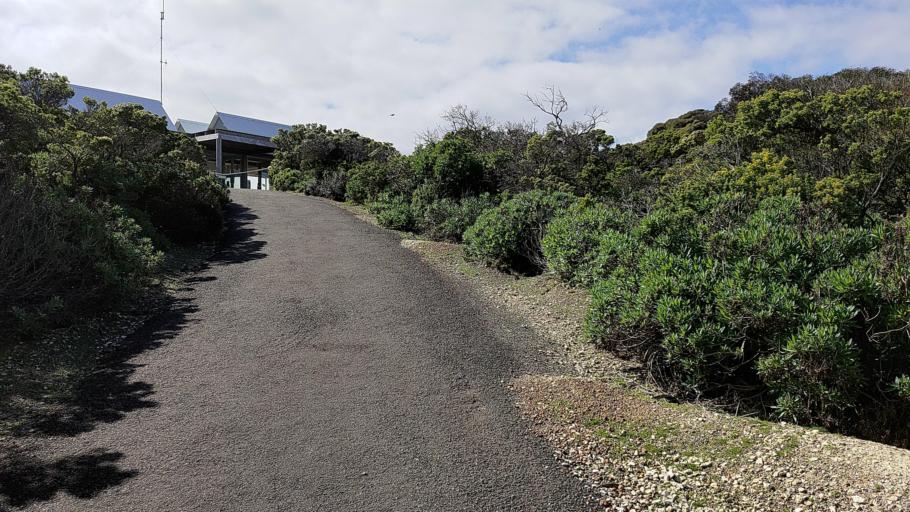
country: AU
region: South Australia
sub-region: Kangaroo Island
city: Kingscote
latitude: -35.9927
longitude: 137.3188
